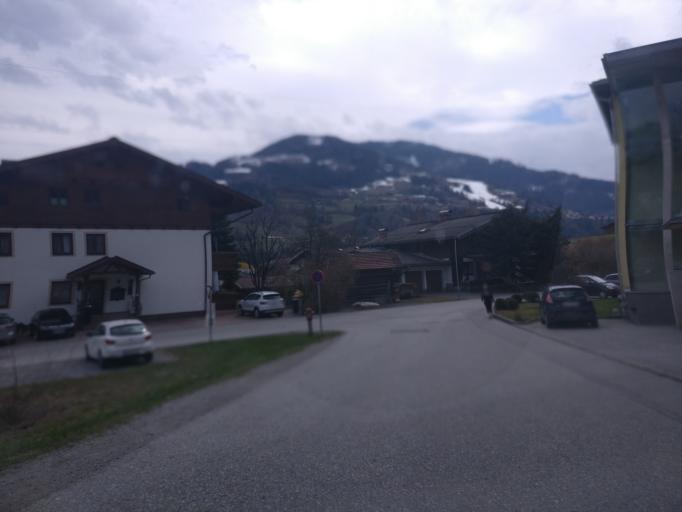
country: AT
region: Salzburg
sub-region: Politischer Bezirk Sankt Johann im Pongau
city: Sankt Johann im Pongau
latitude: 47.3412
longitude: 13.1880
